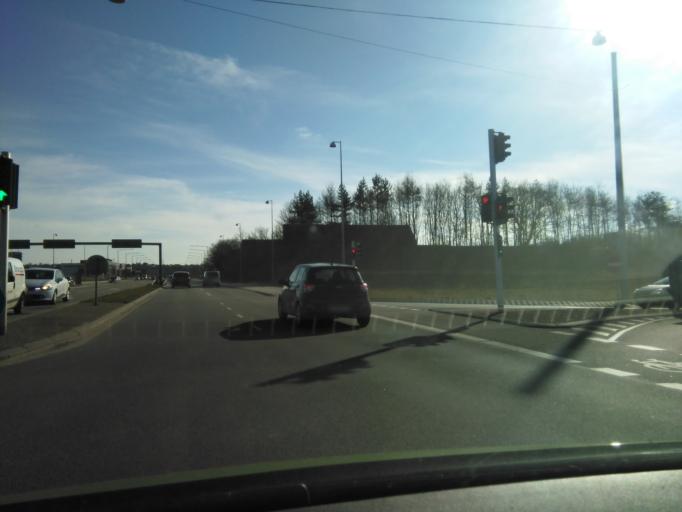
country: DK
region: Central Jutland
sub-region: Arhus Kommune
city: Stavtrup
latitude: 56.1356
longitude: 10.1560
